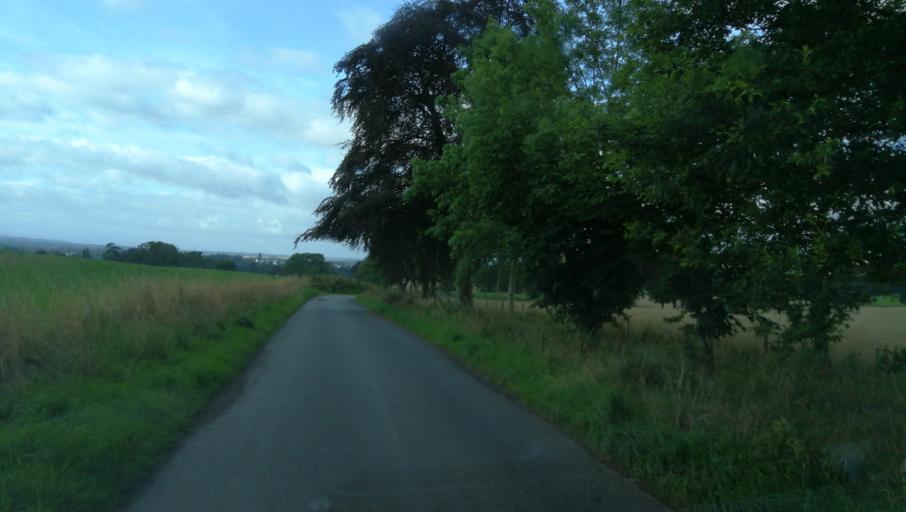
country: GB
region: Scotland
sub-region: Perth and Kinross
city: Blairgowrie
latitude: 56.6014
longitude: -3.3186
